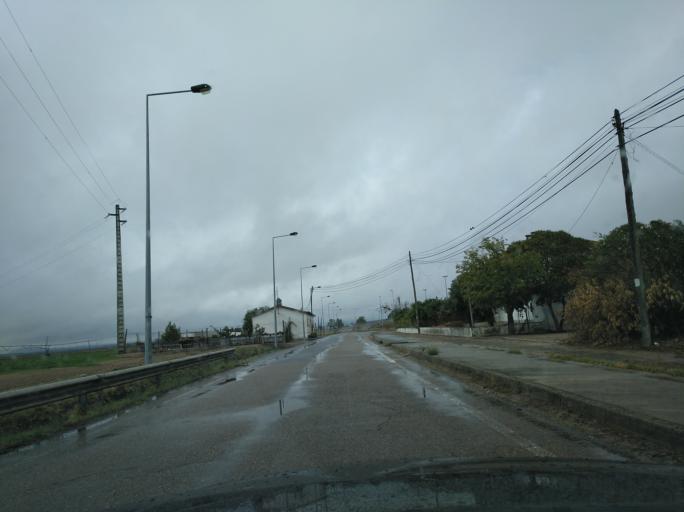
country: ES
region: Extremadura
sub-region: Provincia de Badajoz
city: Badajoz
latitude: 38.8824
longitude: -7.0492
